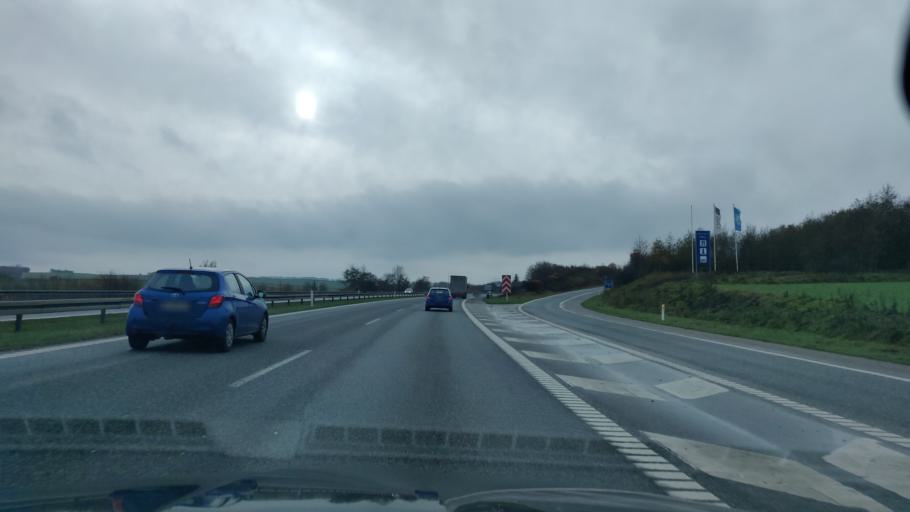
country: DK
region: North Denmark
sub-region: Alborg Kommune
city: Aalborg
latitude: 56.9973
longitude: 9.9056
